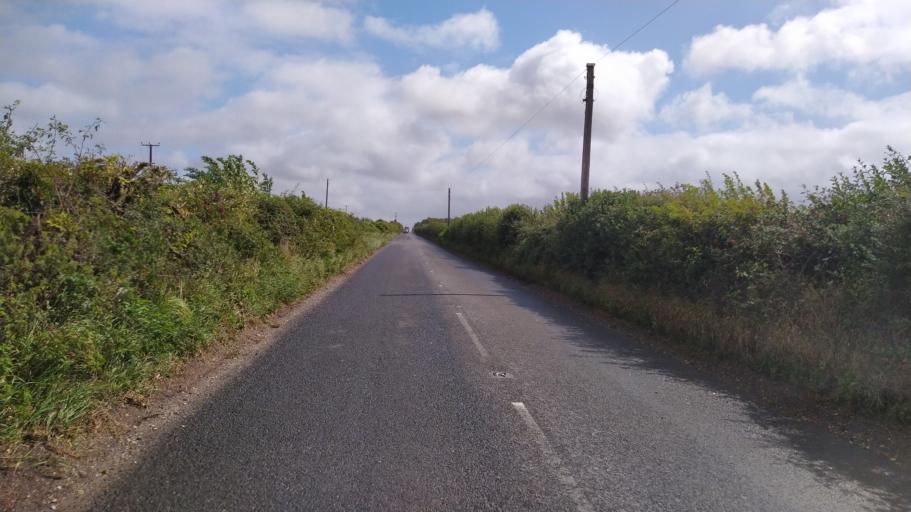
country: GB
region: England
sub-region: Wiltshire
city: Bower Chalke
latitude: 50.9494
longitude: -1.9938
